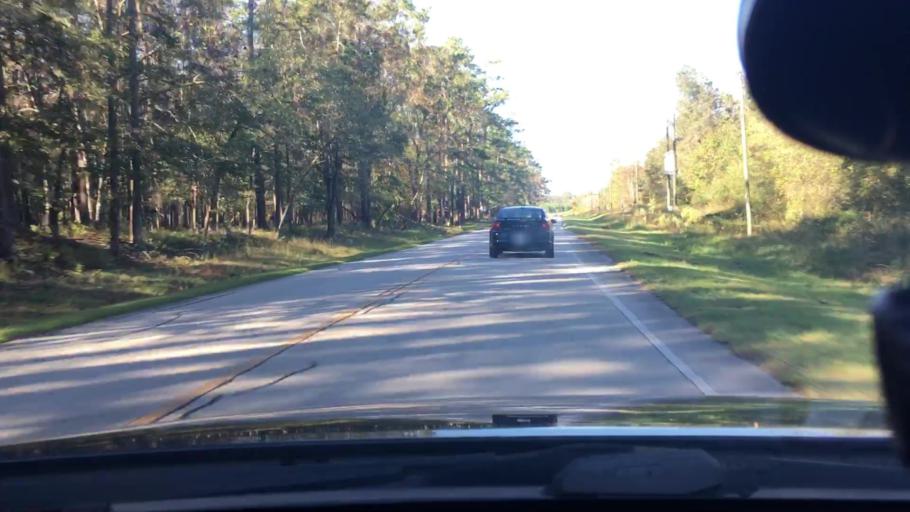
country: US
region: North Carolina
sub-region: Craven County
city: Vanceboro
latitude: 35.2760
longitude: -77.1533
